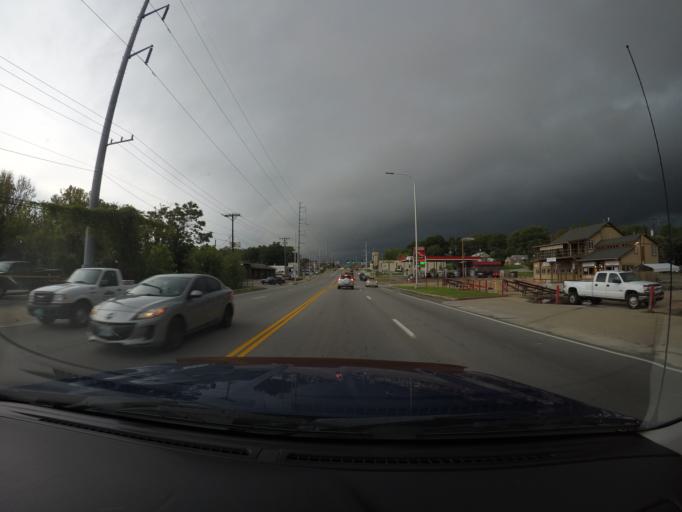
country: US
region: Missouri
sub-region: Jackson County
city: Sugar Creek
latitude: 39.1026
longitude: -94.4510
